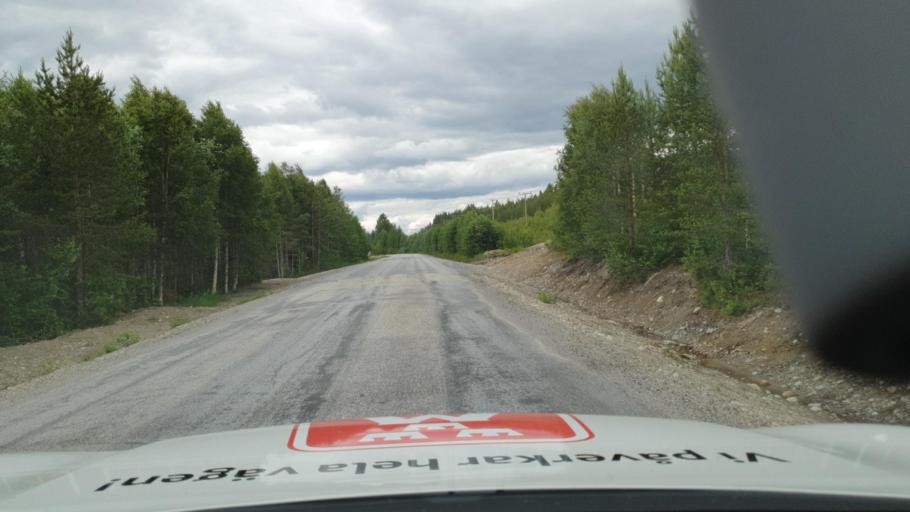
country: SE
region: Vaesterbotten
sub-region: Bjurholms Kommun
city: Bjurholm
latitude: 63.7752
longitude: 19.2382
